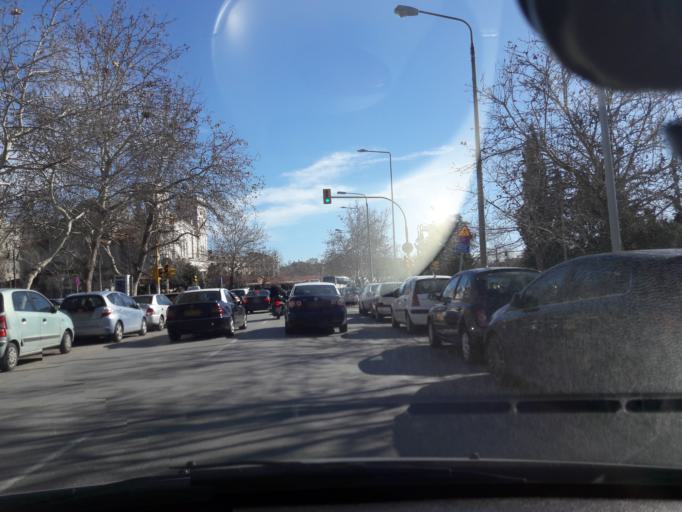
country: GR
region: Central Macedonia
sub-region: Nomos Thessalonikis
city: Kalamaria
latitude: 40.5988
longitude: 22.9503
